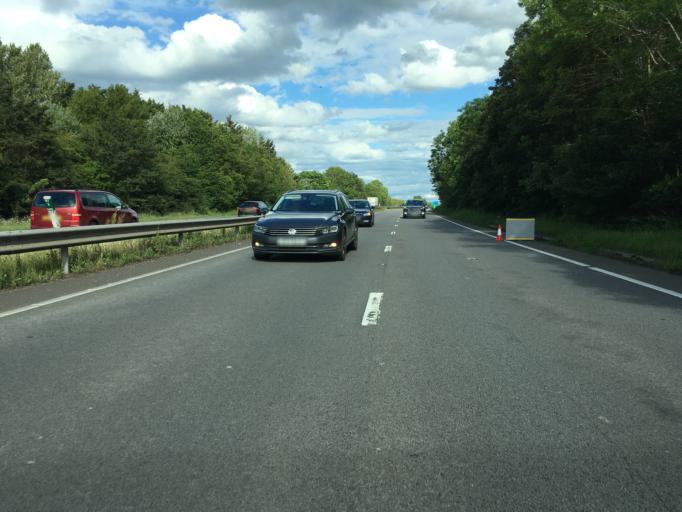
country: GB
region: England
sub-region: Oxfordshire
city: Wheatley
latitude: 51.7476
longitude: -1.1260
